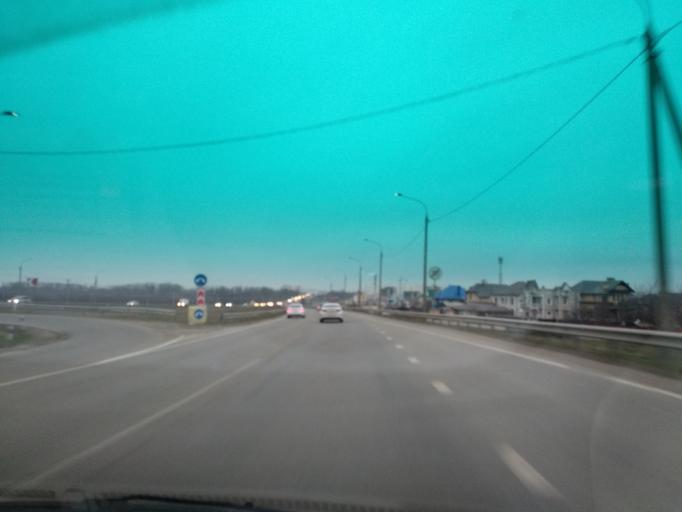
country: RU
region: Krasnodarskiy
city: Pashkovskiy
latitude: 45.0543
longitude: 39.1306
